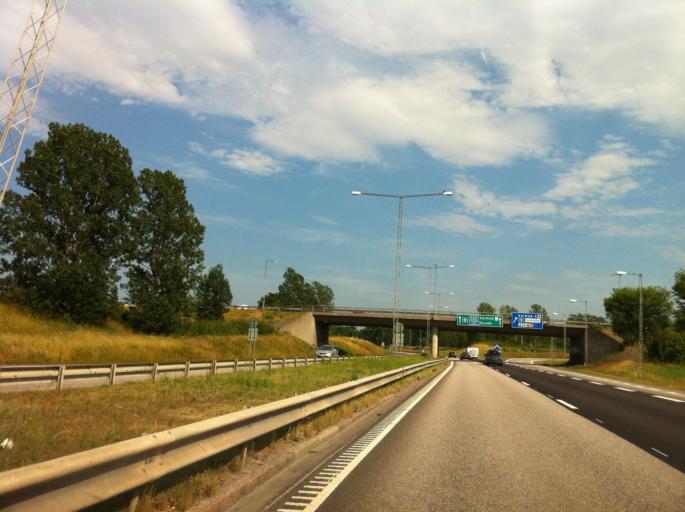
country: SE
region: Kalmar
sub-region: Kalmar Kommun
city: Rinkabyholm
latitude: 56.6693
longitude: 16.2864
